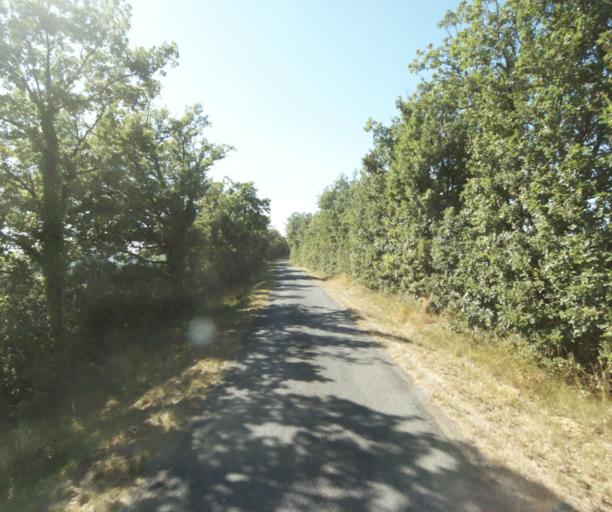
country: FR
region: Midi-Pyrenees
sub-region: Departement de la Haute-Garonne
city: Saint-Felix-Lauragais
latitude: 43.5207
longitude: 1.9133
